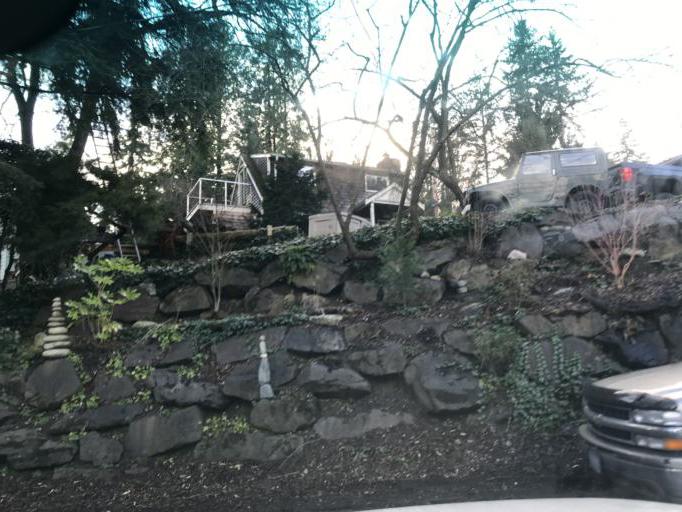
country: US
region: Washington
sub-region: King County
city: Lake Forest Park
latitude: 47.7189
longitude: -122.3036
